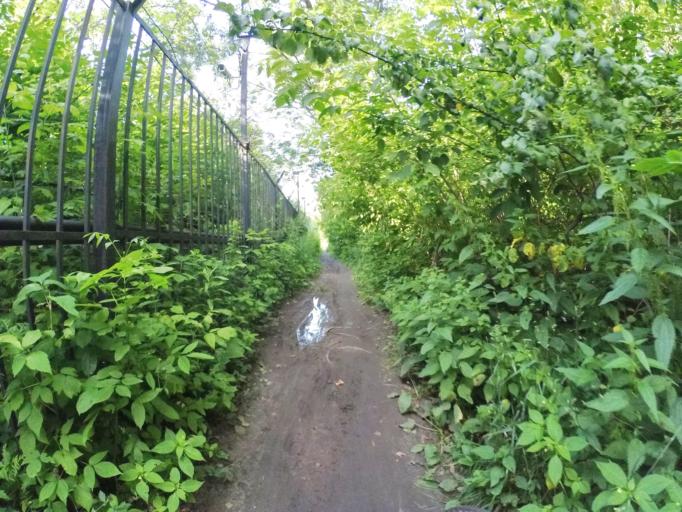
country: RU
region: Moscow
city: Pokrovskoye-Streshnevo
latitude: 55.8141
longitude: 37.4502
